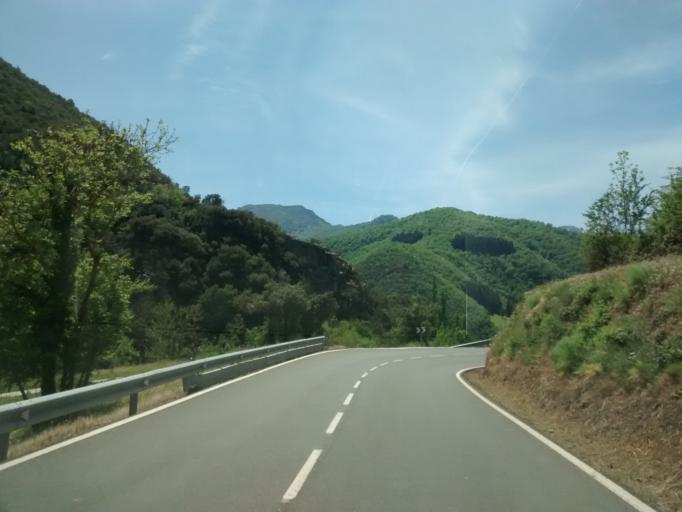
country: ES
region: Cantabria
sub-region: Provincia de Cantabria
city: Potes
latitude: 43.1037
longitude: -4.6425
